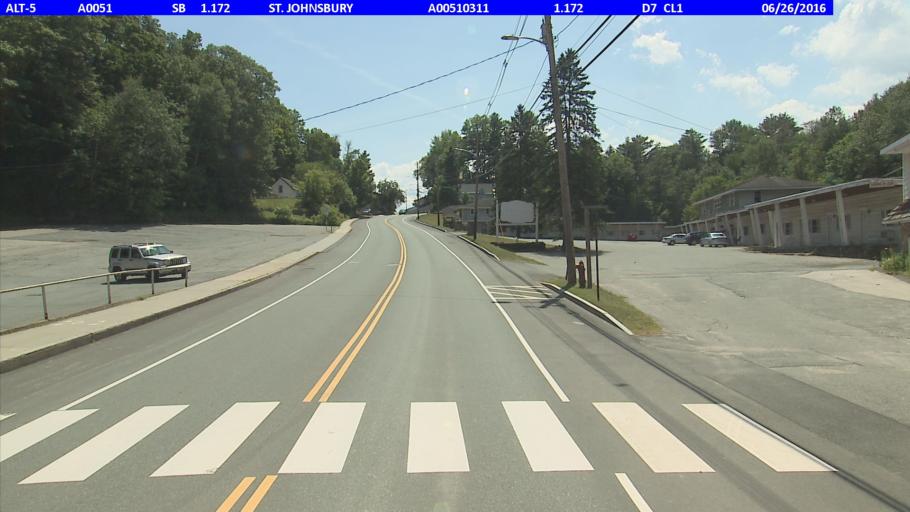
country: US
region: Vermont
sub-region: Caledonia County
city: St Johnsbury
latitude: 44.4274
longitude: -72.0186
